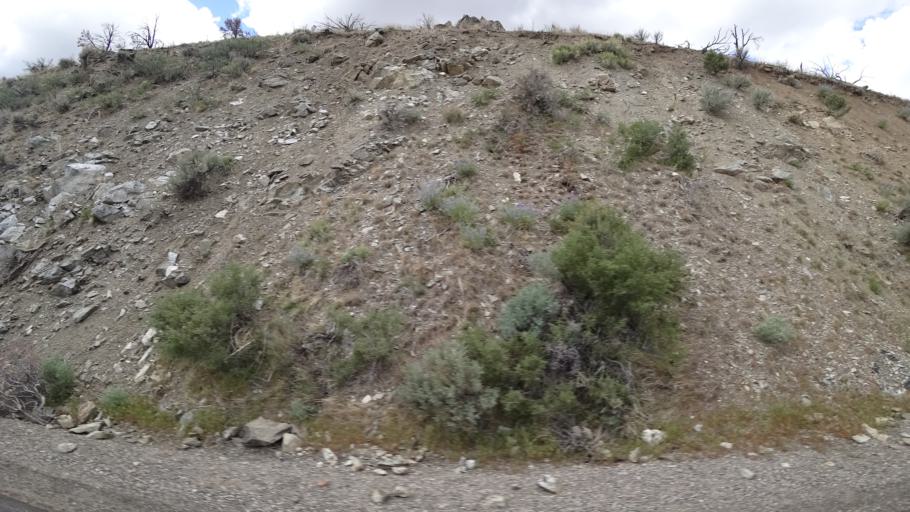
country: US
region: Nevada
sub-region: Lyon County
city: Smith Valley
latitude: 38.6632
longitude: -119.5414
